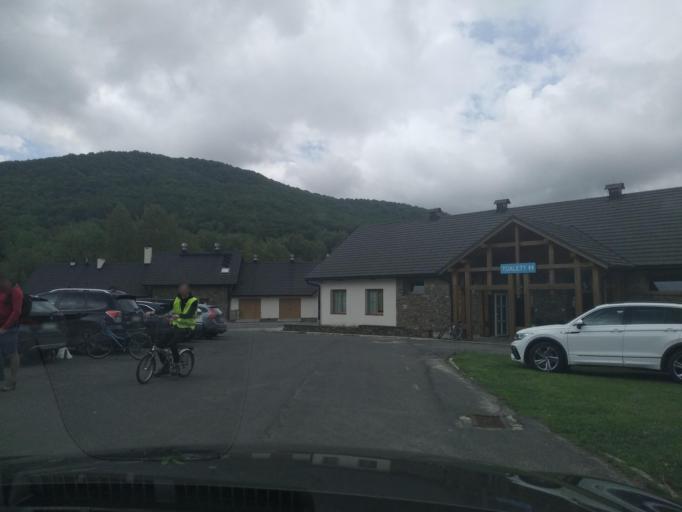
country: PL
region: Subcarpathian Voivodeship
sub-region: Powiat bieszczadzki
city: Lutowiska
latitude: 49.0662
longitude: 22.6798
